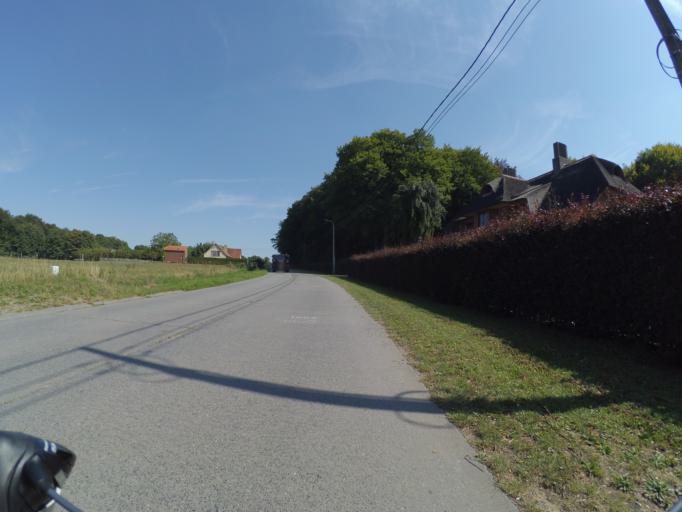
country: BE
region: Flanders
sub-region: Provincie Oost-Vlaanderen
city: Ronse
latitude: 50.7649
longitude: 3.5335
